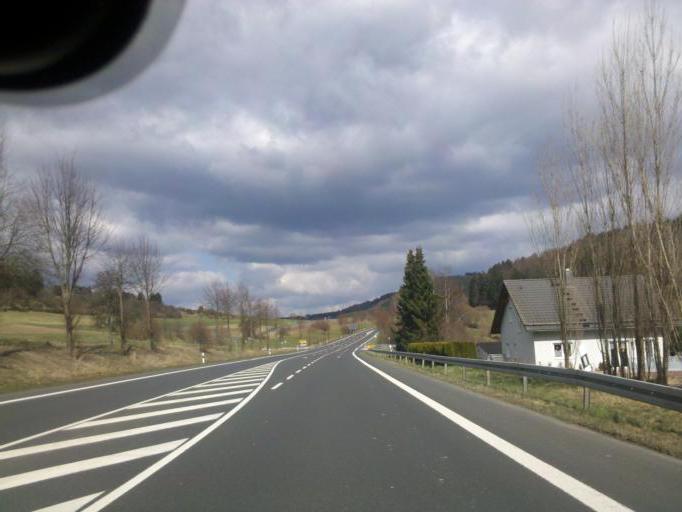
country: DE
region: Hesse
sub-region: Regierungsbezirk Giessen
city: Siegbach
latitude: 50.8250
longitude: 8.3774
